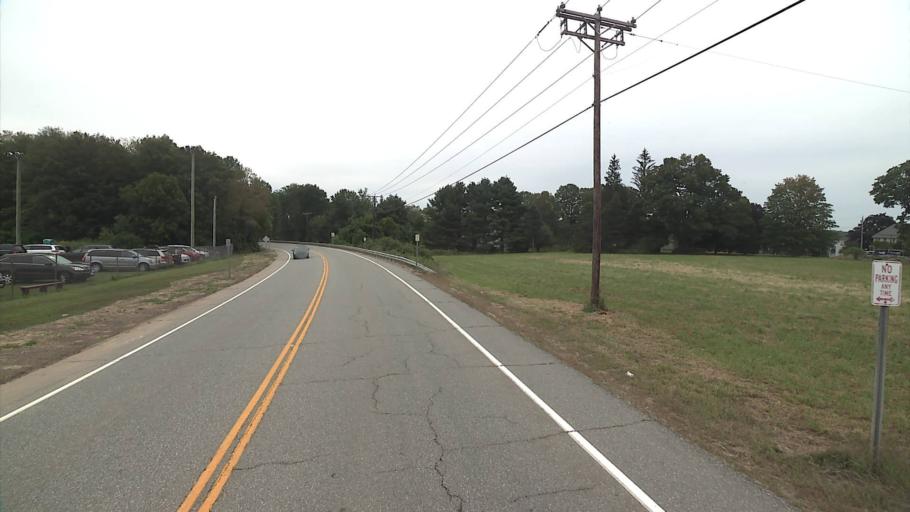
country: US
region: Connecticut
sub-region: Tolland County
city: Hebron
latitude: 41.6750
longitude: -72.4092
